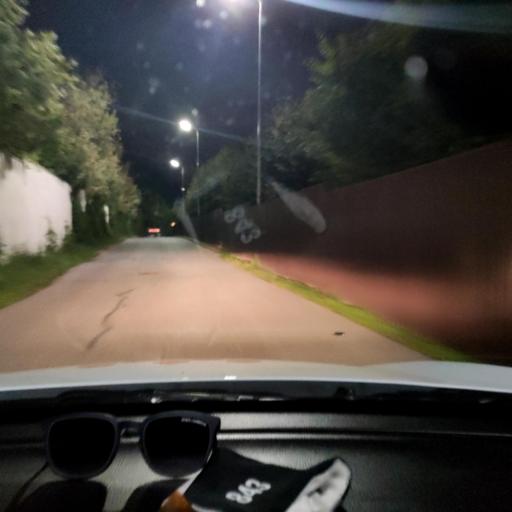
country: RU
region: Tatarstan
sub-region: Gorod Kazan'
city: Kazan
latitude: 55.7413
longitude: 49.1659
